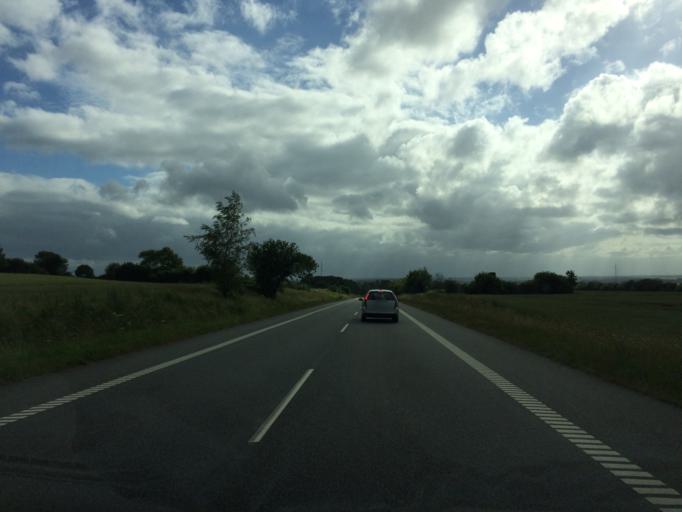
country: DK
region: South Denmark
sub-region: Sonderborg Kommune
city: Augustenborg
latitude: 54.9712
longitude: 9.9421
